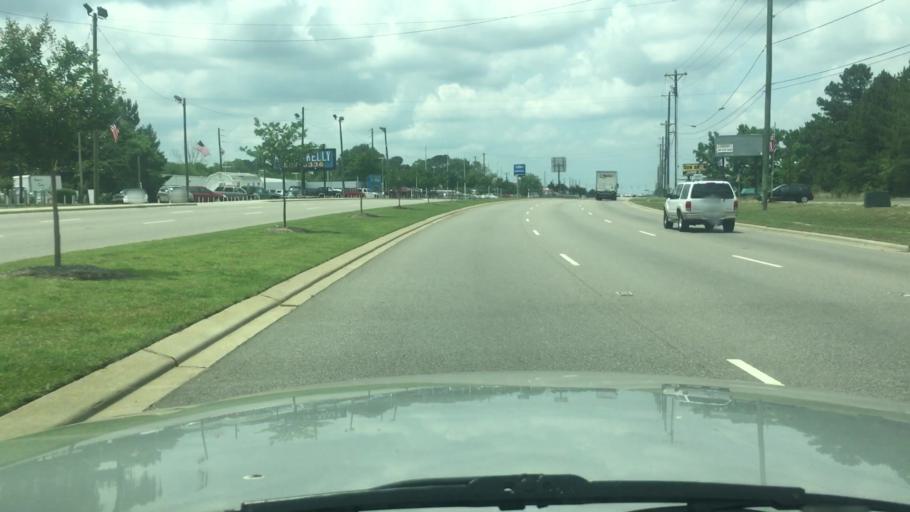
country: US
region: North Carolina
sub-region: Cumberland County
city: Fort Bragg
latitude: 35.0888
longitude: -78.9532
